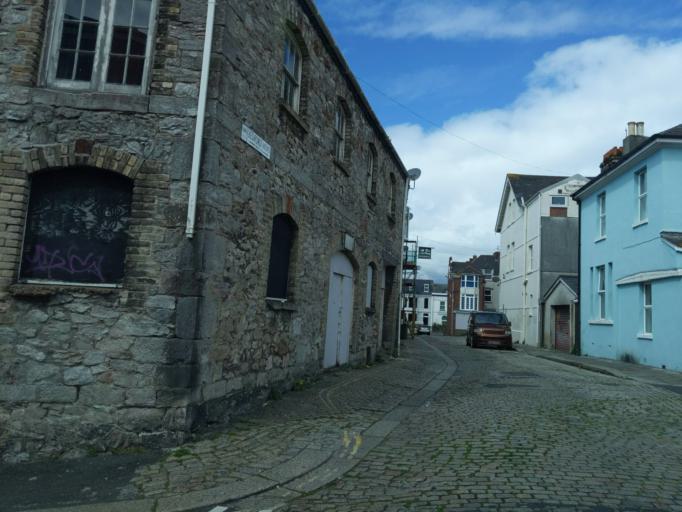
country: GB
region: England
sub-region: Plymouth
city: Plymouth
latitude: 50.3770
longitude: -4.1344
